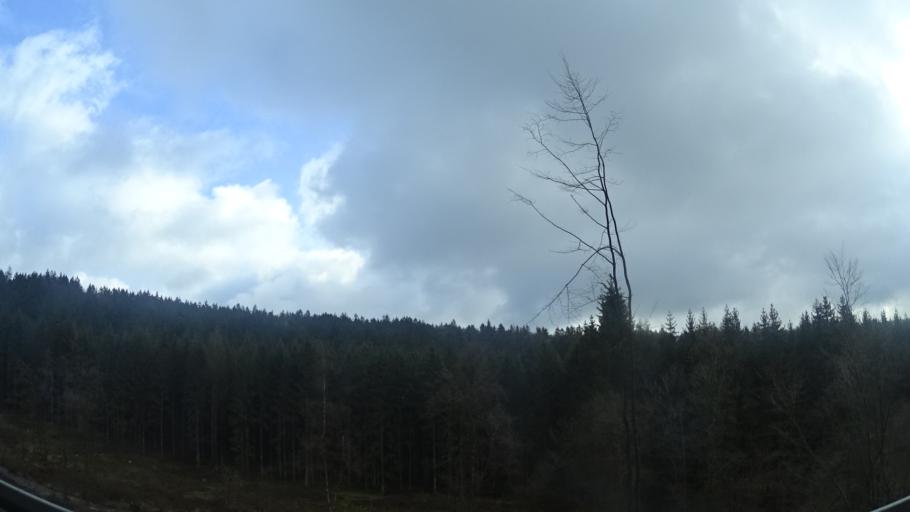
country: DE
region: Rheinland-Pfalz
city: Borfink
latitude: 49.6939
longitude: 7.0807
